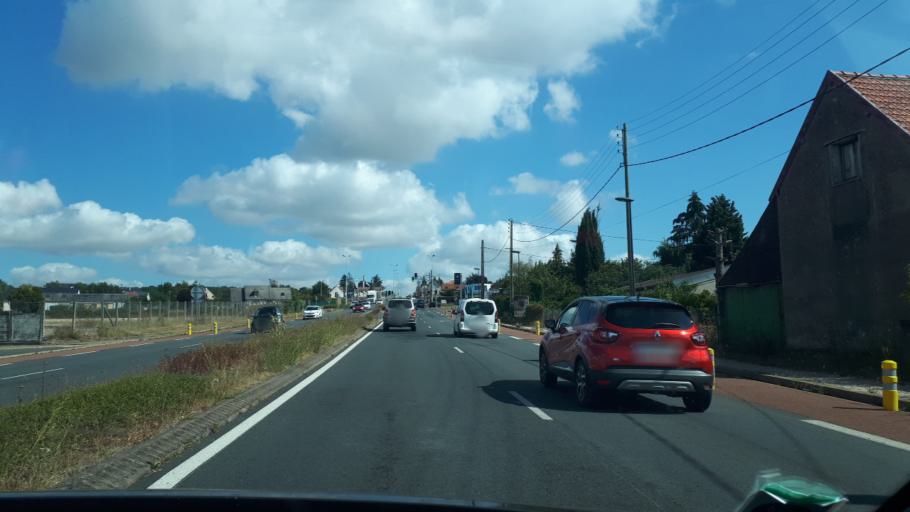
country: FR
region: Centre
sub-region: Departement du Loir-et-Cher
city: Saint-Ouen
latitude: 47.8093
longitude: 1.0732
